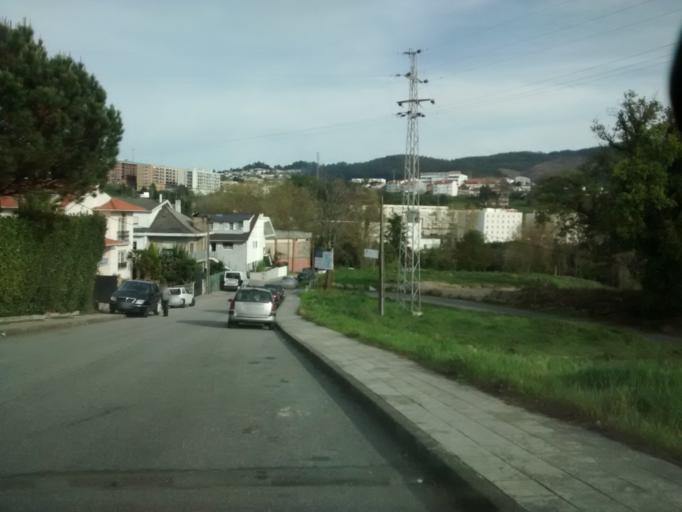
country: PT
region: Braga
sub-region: Guimaraes
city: Guimaraes
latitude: 41.4552
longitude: -8.2896
